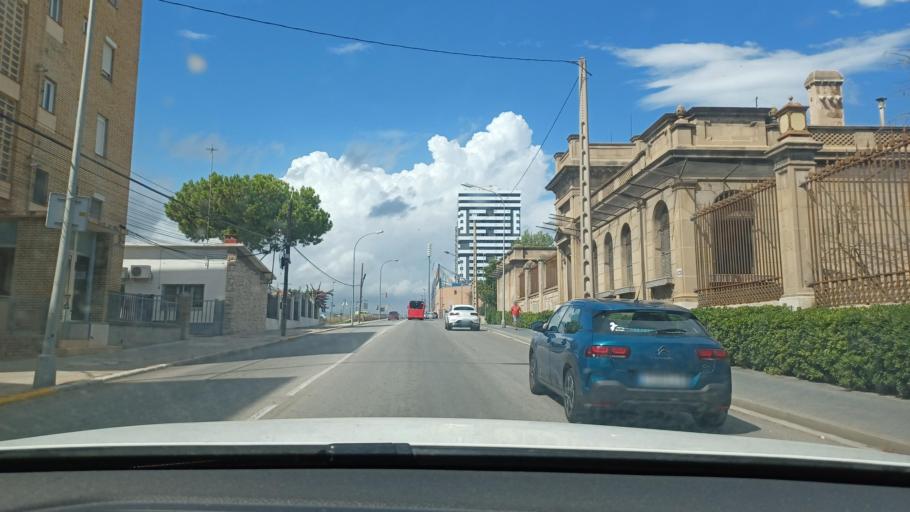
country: ES
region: Catalonia
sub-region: Provincia de Tarragona
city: Tarragona
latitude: 41.1147
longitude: 1.2381
